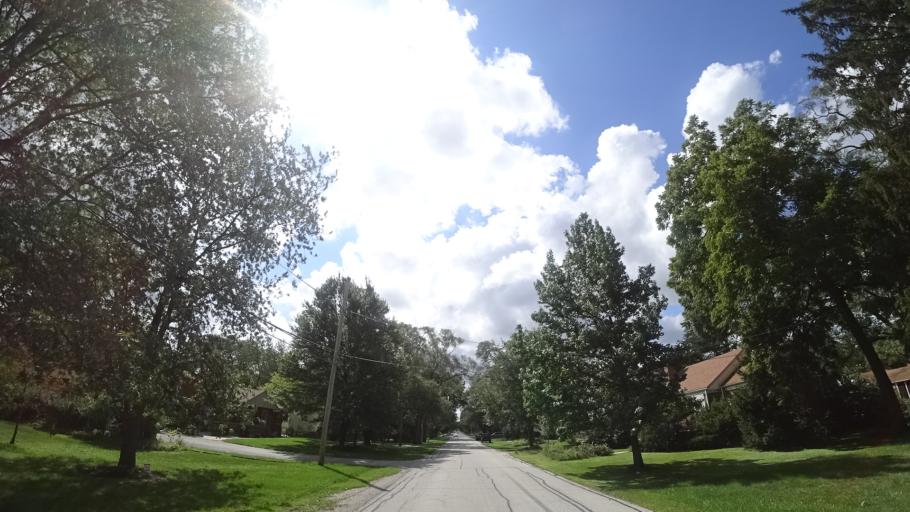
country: US
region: Illinois
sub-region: Cook County
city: Tinley Park
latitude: 41.5713
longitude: -87.7793
